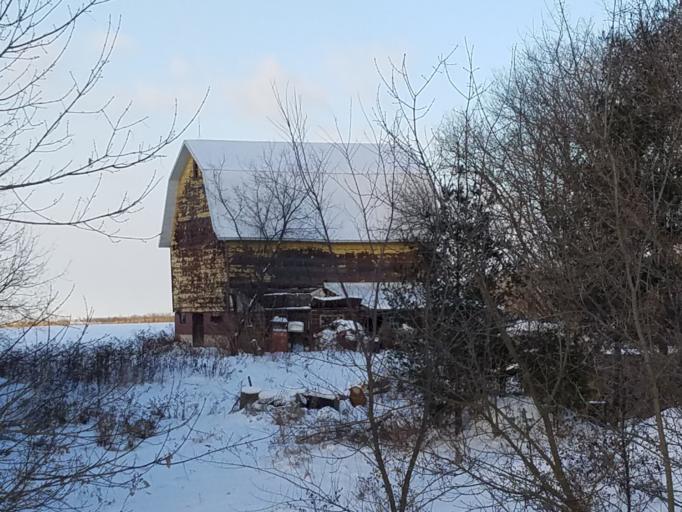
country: US
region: Wisconsin
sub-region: Clark County
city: Loyal
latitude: 44.6224
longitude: -90.4553
